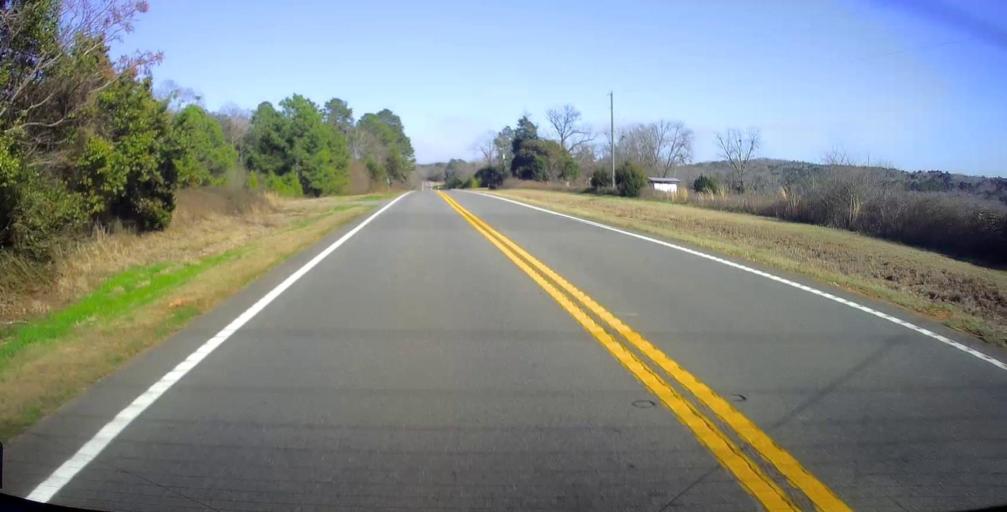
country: US
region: Georgia
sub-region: Macon County
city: Oglethorpe
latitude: 32.3516
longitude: -84.1675
